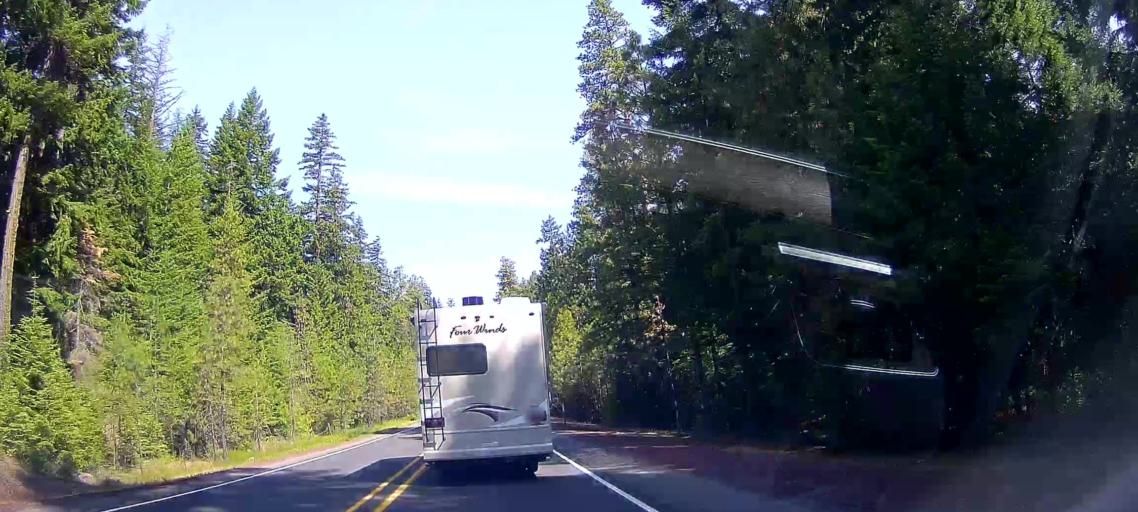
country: US
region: Oregon
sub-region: Jefferson County
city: Warm Springs
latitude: 45.0758
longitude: -121.5369
